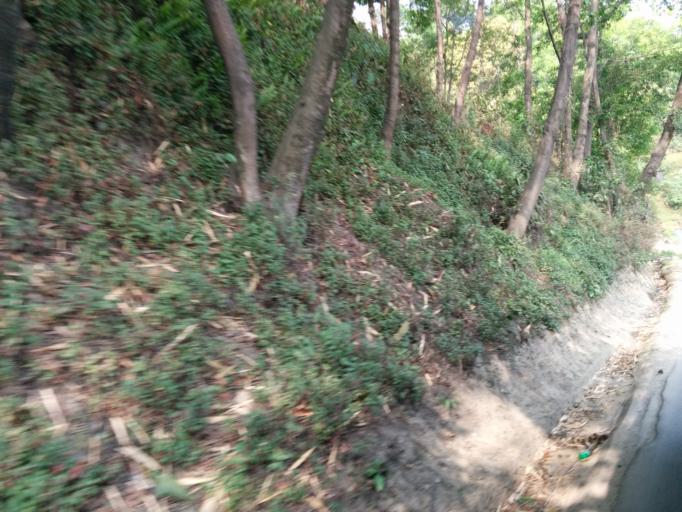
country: NP
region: Central Region
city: Kirtipur
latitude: 27.7170
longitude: 85.1576
